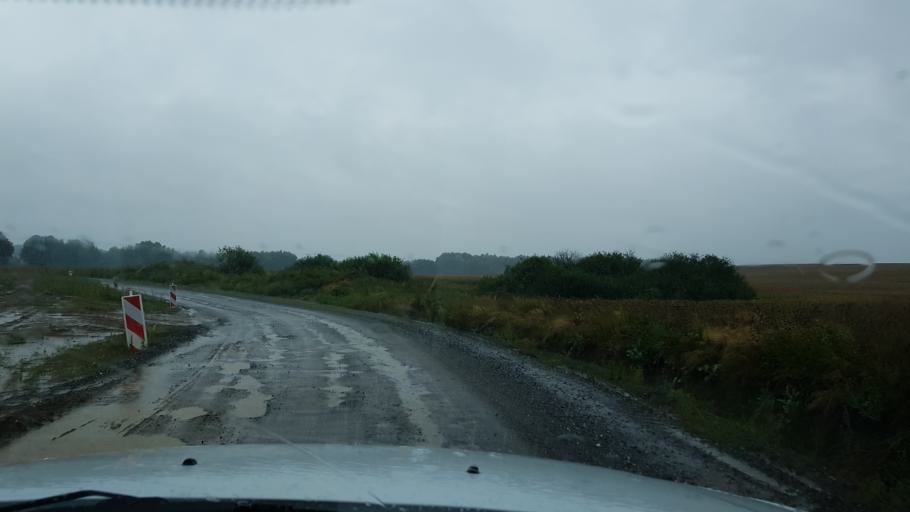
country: PL
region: West Pomeranian Voivodeship
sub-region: Powiat kolobrzeski
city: Grzybowo
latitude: 54.0776
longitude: 15.5142
